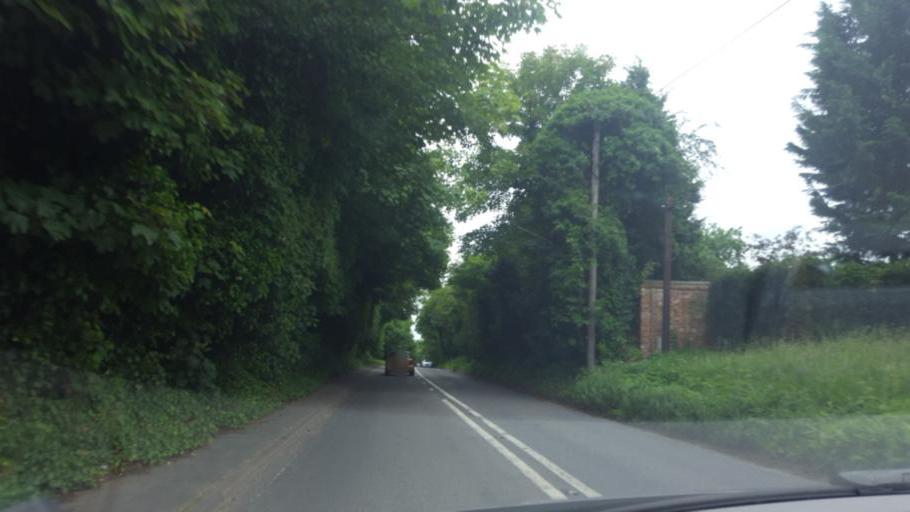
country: GB
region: England
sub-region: Royal Borough of Windsor and Maidenhead
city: Hurley
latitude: 51.5348
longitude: -0.7909
